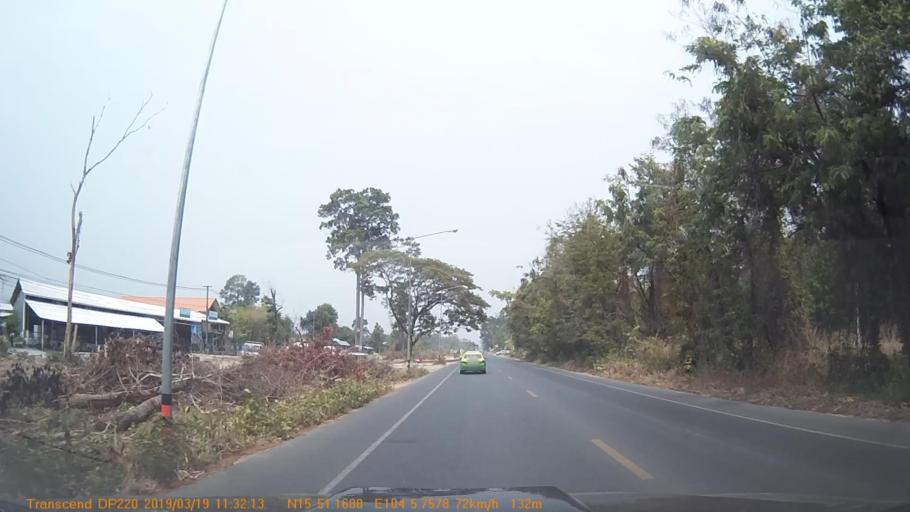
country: TH
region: Yasothon
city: Yasothon
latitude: 15.8530
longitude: 104.0958
